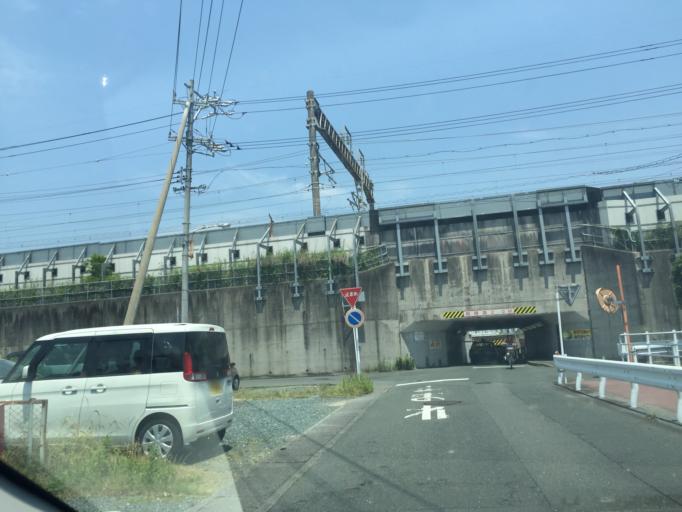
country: JP
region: Shizuoka
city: Kakegawa
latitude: 34.7684
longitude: 138.0125
